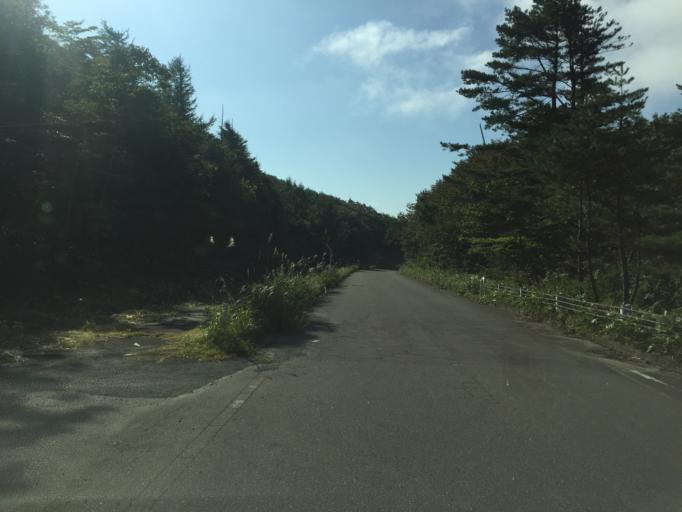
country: JP
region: Fukushima
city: Inawashiro
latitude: 37.4680
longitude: 139.9908
